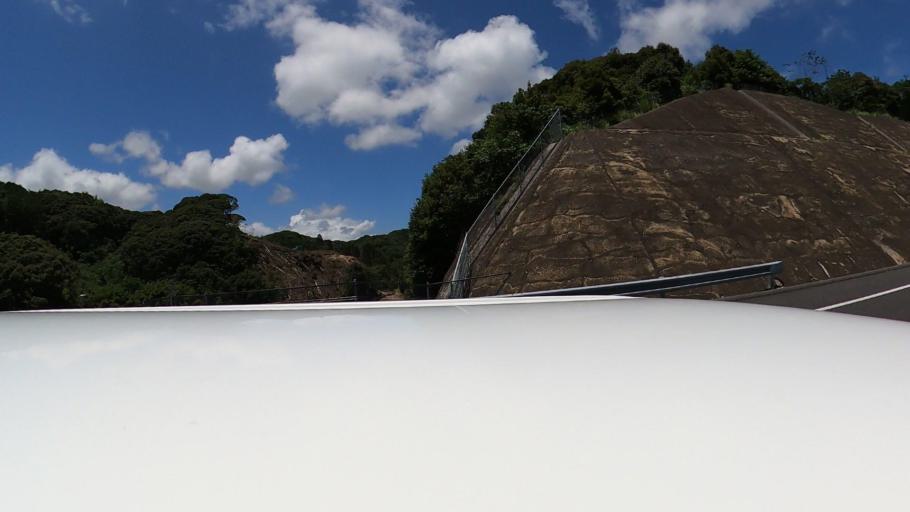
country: JP
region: Miyazaki
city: Nobeoka
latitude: 32.4932
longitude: 131.6546
